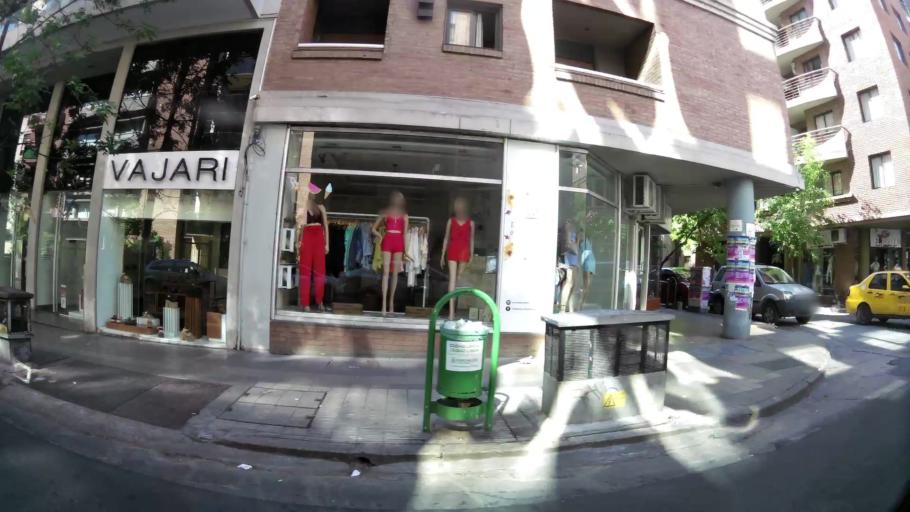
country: AR
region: Cordoba
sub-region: Departamento de Capital
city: Cordoba
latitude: -31.4240
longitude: -64.1843
